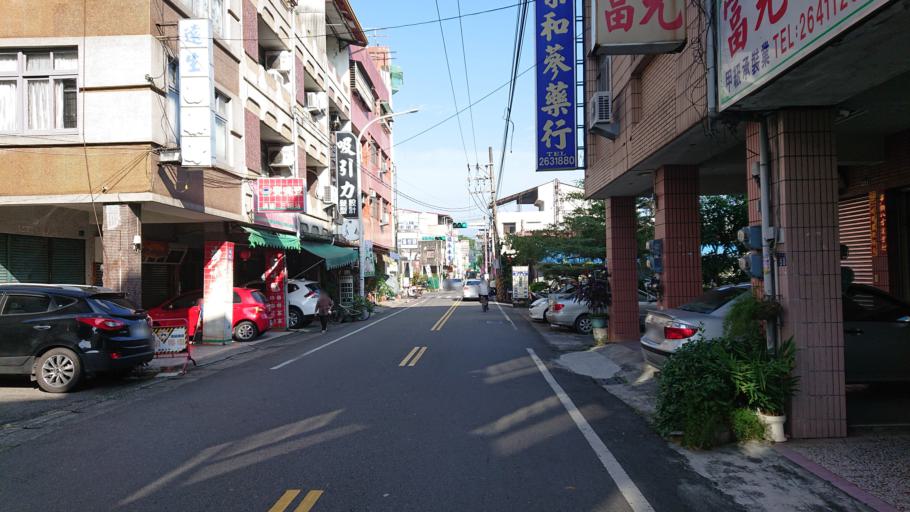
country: TW
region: Taiwan
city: Lugu
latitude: 23.7577
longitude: 120.6852
